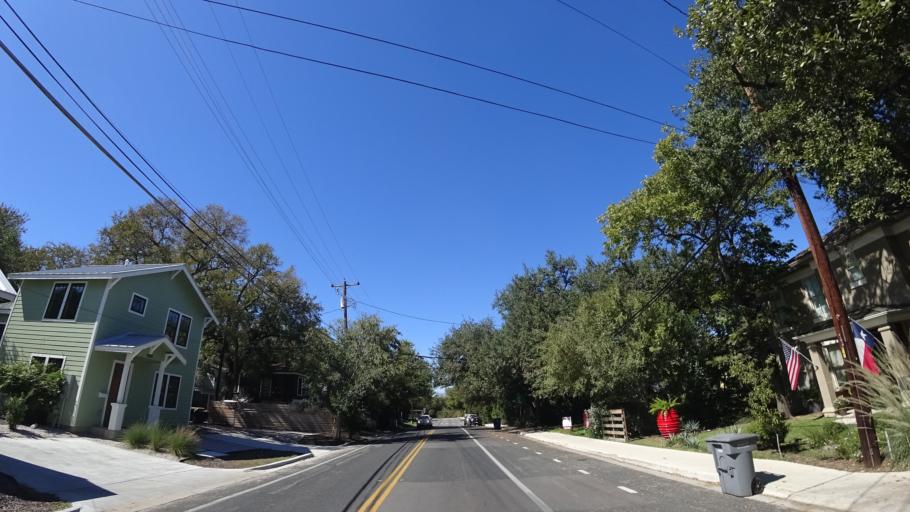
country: US
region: Texas
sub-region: Travis County
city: Austin
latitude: 30.2432
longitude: -97.7413
